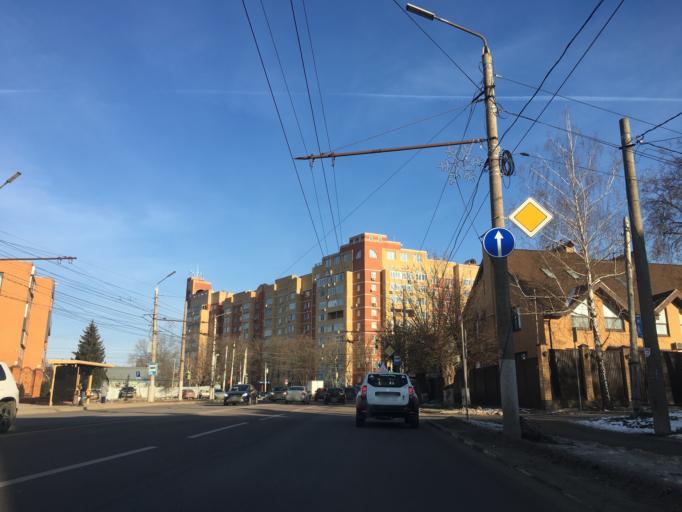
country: RU
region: Tula
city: Tula
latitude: 54.1887
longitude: 37.5820
